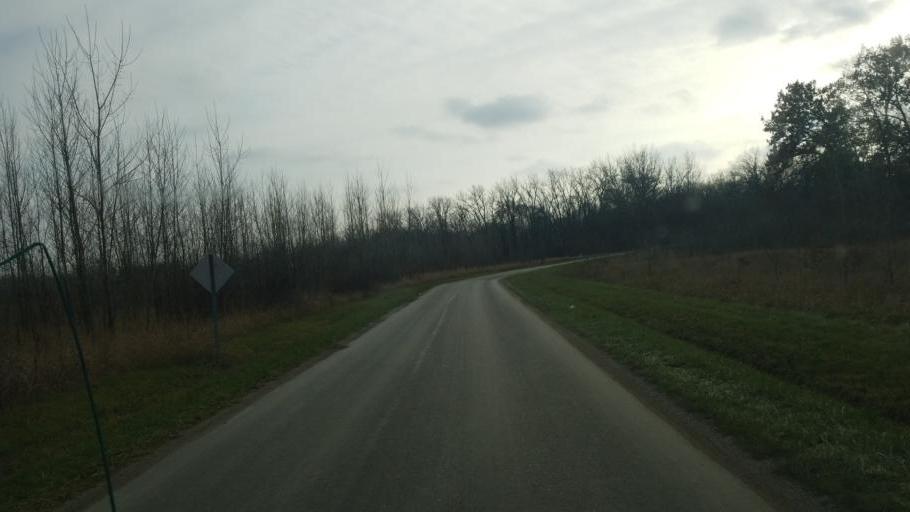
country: US
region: Indiana
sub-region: Adams County
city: Geneva
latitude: 40.6185
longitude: -84.9636
